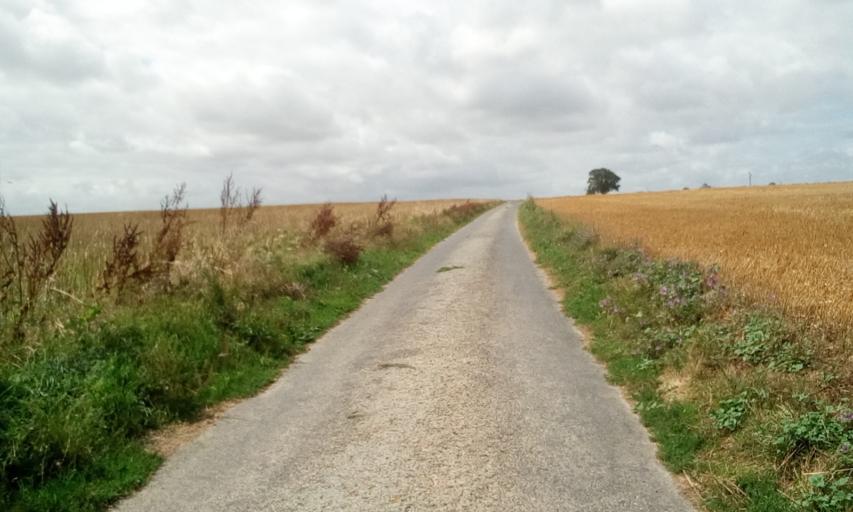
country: FR
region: Lower Normandy
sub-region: Departement du Calvados
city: Cheux
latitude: 49.1821
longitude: -0.5554
